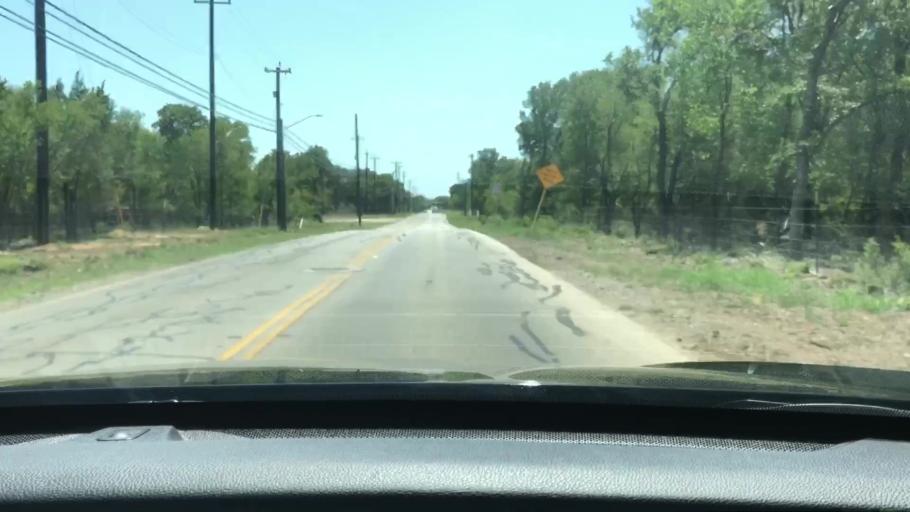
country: US
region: Texas
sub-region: Bexar County
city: Helotes
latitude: 29.5571
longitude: -98.6558
